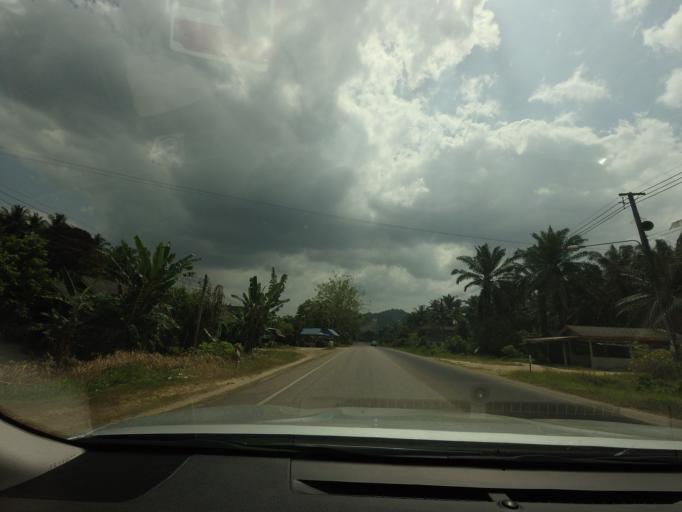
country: TH
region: Phangnga
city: Ban Ao Nang
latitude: 8.0986
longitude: 98.8027
